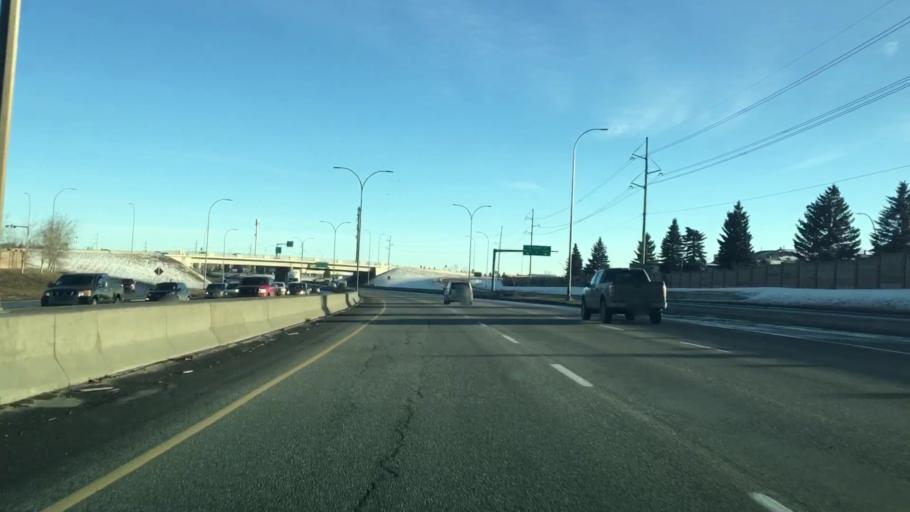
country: CA
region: Alberta
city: Calgary
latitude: 50.9824
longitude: -114.0195
